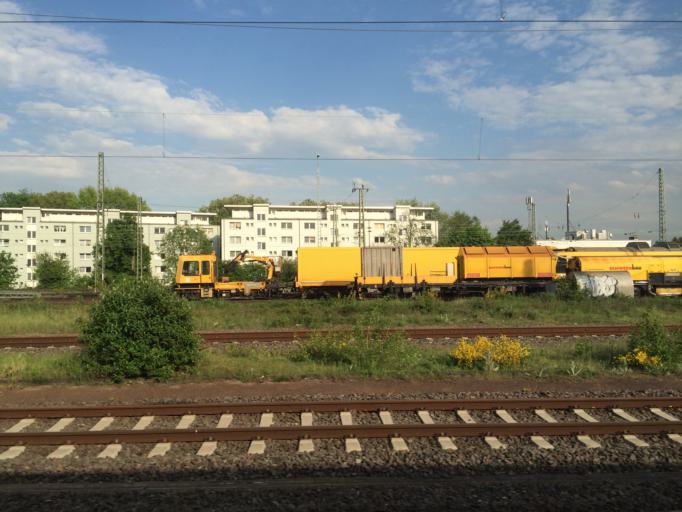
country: DE
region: North Rhine-Westphalia
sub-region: Regierungsbezirk Koln
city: Buchheim
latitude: 50.9608
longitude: 7.0157
